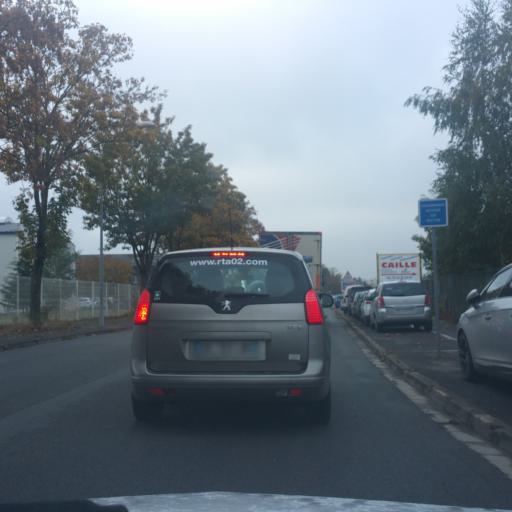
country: FR
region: Picardie
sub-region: Departement de l'Aisne
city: Laon
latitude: 49.5740
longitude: 3.6470
